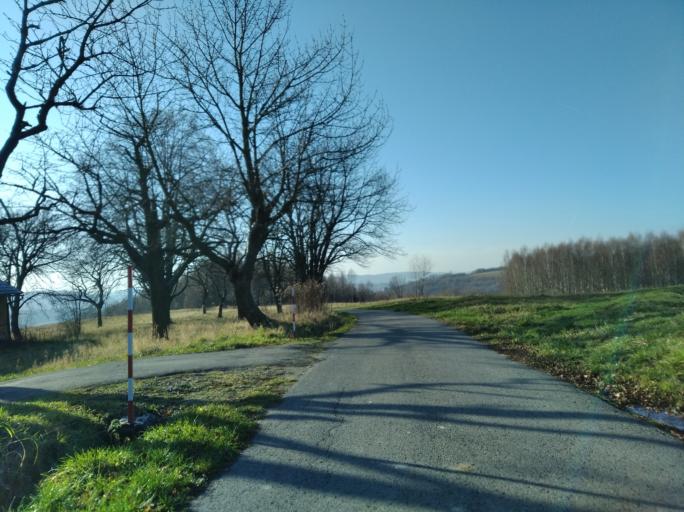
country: PL
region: Subcarpathian Voivodeship
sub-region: Powiat strzyzowski
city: Strzyzow
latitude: 49.8811
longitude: 21.8329
